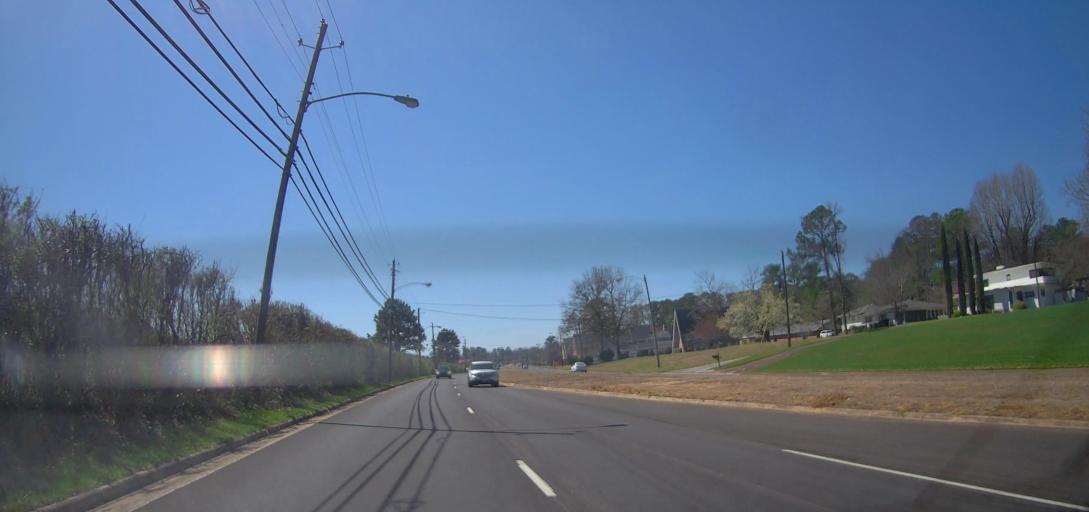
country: US
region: Alabama
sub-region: Etowah County
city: Gadsden
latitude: 33.9783
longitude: -86.0090
